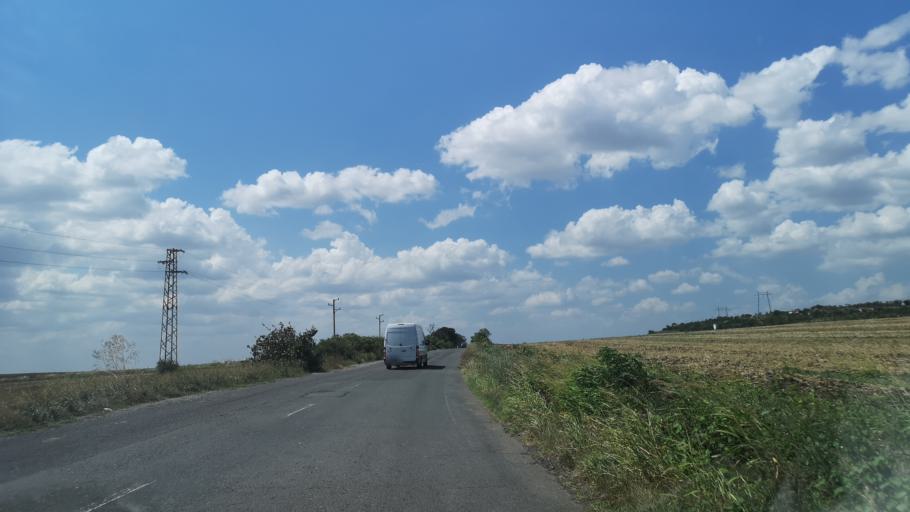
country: BG
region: Burgas
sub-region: Obshtina Kameno
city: Kameno
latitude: 42.6231
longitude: 27.3410
